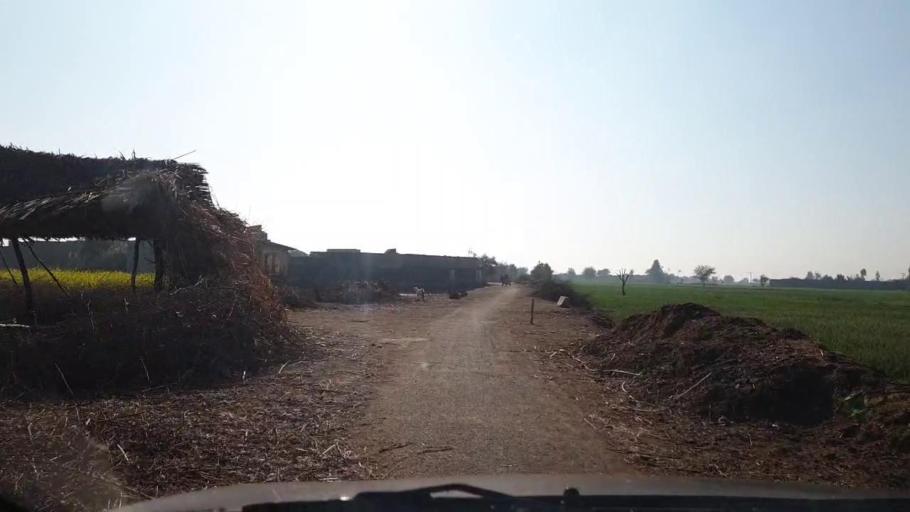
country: PK
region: Sindh
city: Sinjhoro
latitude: 26.0030
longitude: 68.7768
